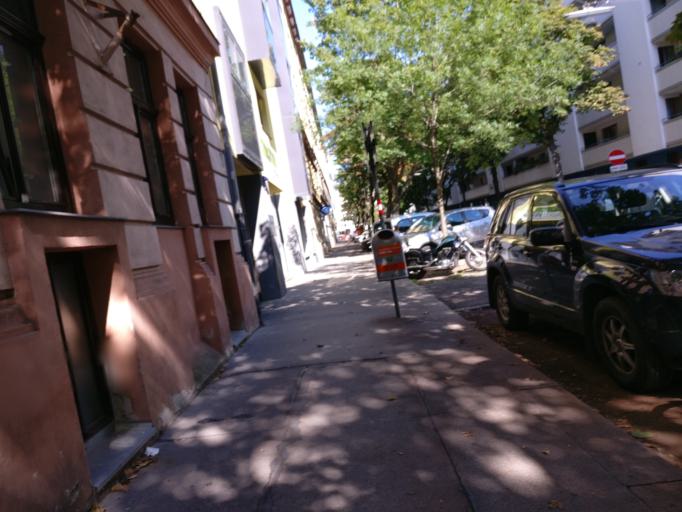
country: AT
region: Vienna
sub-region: Wien Stadt
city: Vienna
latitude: 48.2355
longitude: 16.3795
